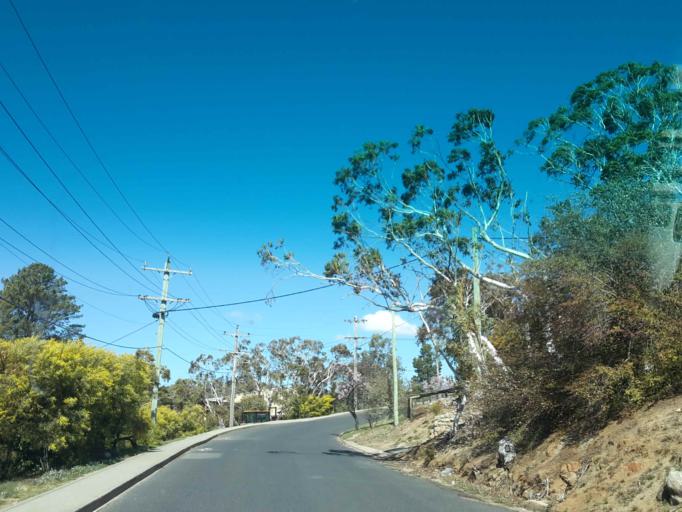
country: AU
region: New South Wales
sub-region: Snowy River
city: Jindabyne
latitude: -36.4185
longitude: 148.6269
